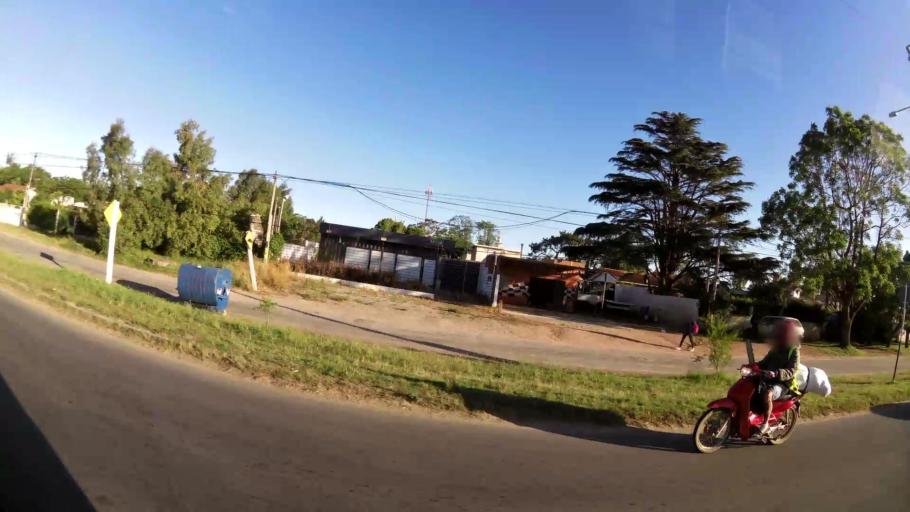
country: UY
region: Canelones
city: Paso de Carrasco
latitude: -34.8541
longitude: -56.0414
